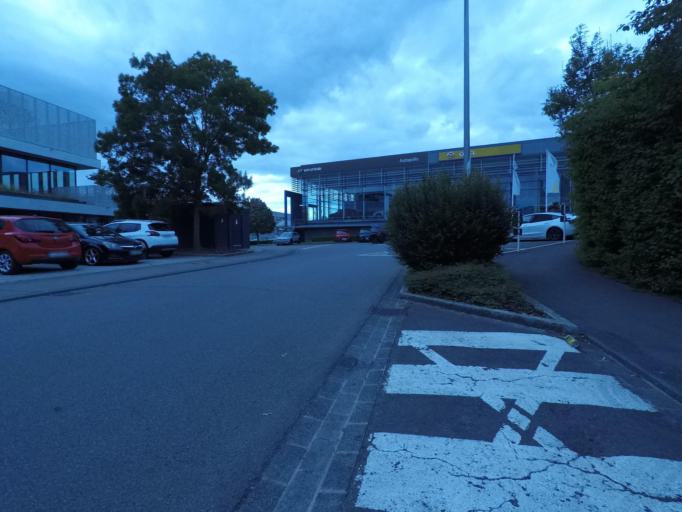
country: LU
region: Luxembourg
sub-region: Canton de Luxembourg
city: Strassen
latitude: 49.6104
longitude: 6.0793
